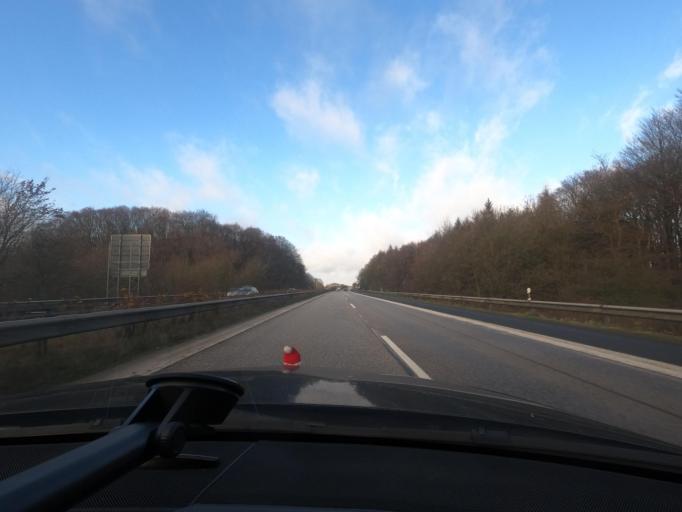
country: DE
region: Schleswig-Holstein
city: Neu Duvenstedt
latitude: 54.3745
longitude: 9.6619
